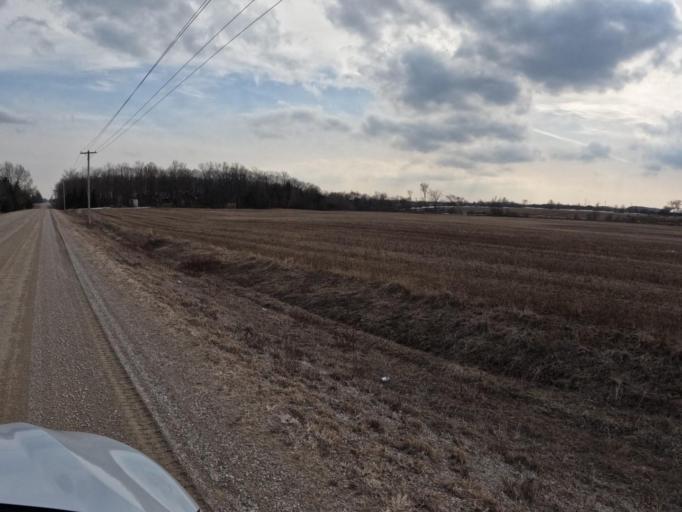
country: CA
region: Ontario
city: Shelburne
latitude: 43.9252
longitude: -80.3071
